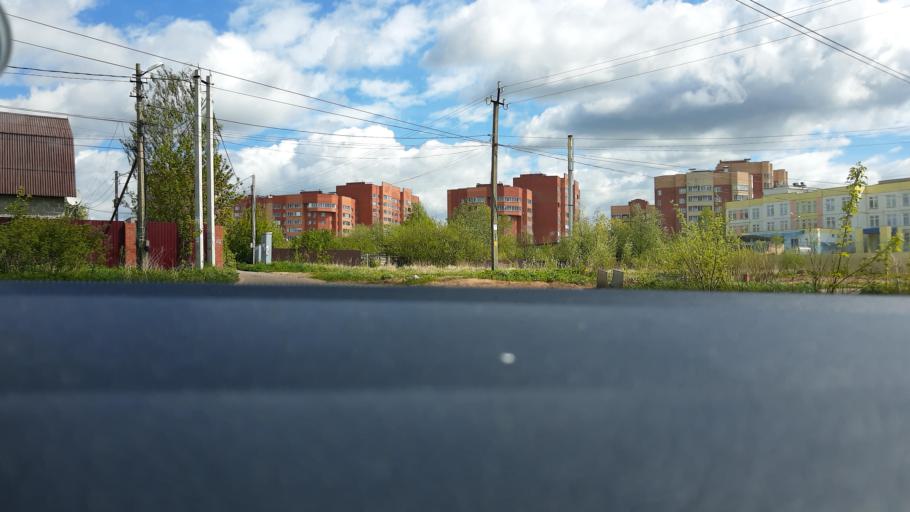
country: RU
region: Moskovskaya
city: Dmitrov
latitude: 56.3555
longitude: 37.5446
